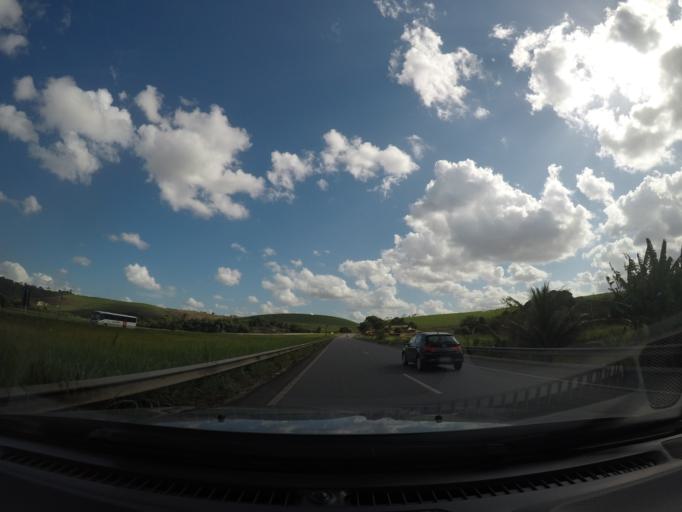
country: BR
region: Pernambuco
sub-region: Joaquim Nabuco
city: Joaquim Nabuco
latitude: -8.6394
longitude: -35.5608
